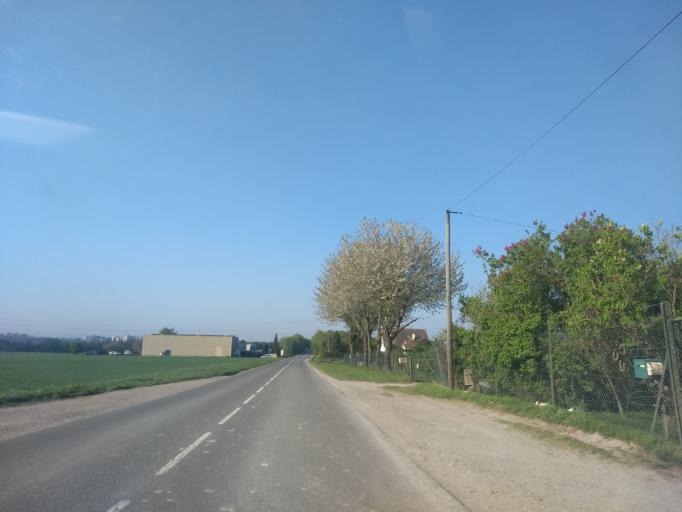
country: FR
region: Picardie
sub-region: Departement de la Somme
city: Rivery
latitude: 49.9258
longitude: 2.3353
